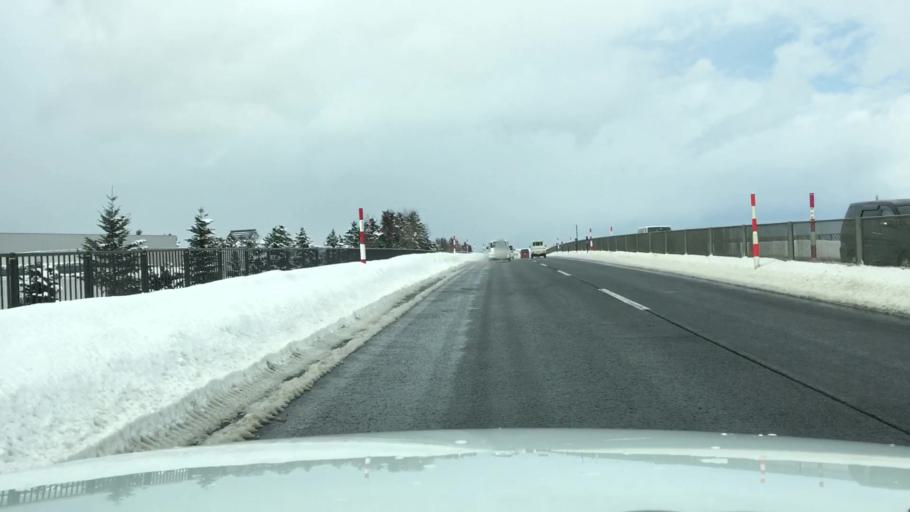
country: JP
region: Aomori
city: Hirosaki
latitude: 40.5881
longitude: 140.5067
